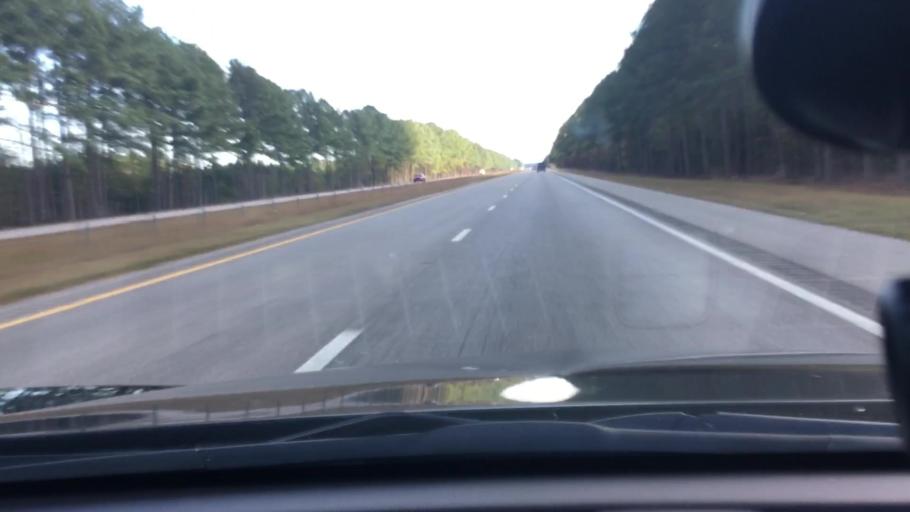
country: US
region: North Carolina
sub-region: Pitt County
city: Farmville
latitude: 35.6496
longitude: -77.7386
